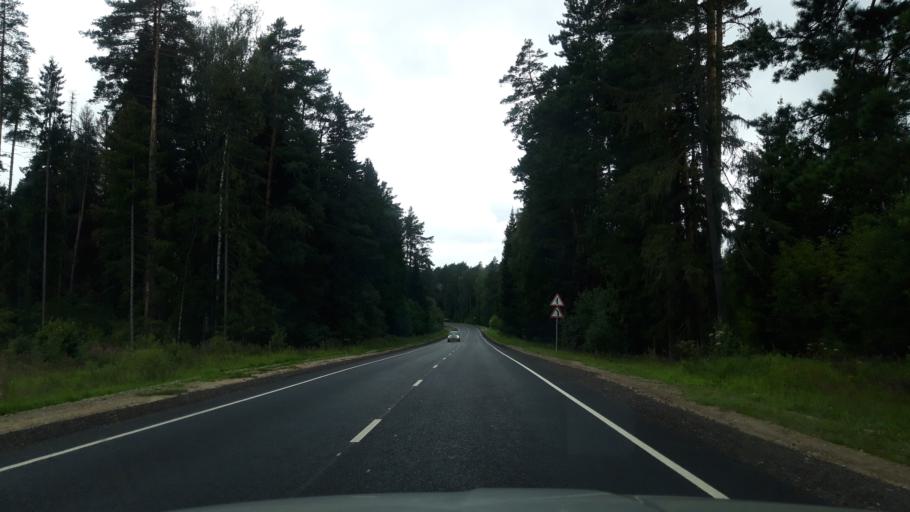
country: RU
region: Moskovskaya
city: Solnechnogorsk
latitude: 56.0967
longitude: 36.9351
